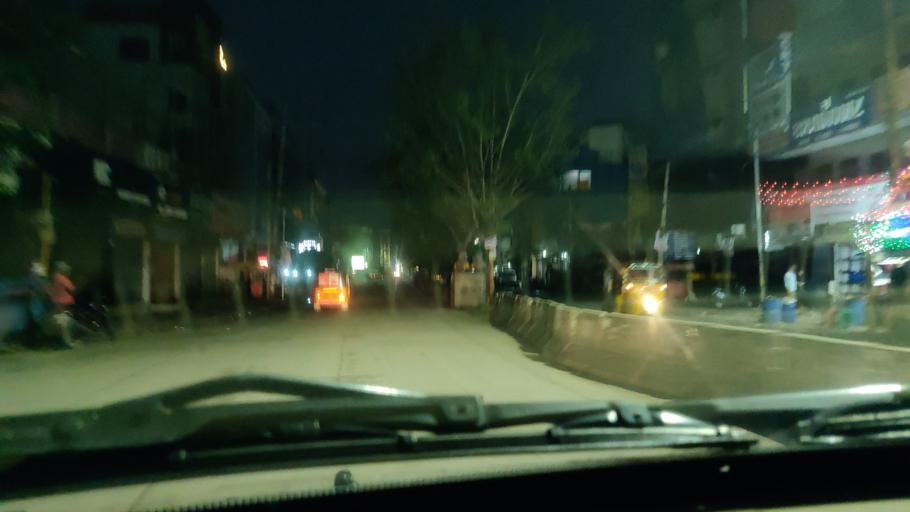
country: IN
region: Telangana
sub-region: Hyderabad
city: Hyderabad
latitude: 17.4389
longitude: 78.4483
